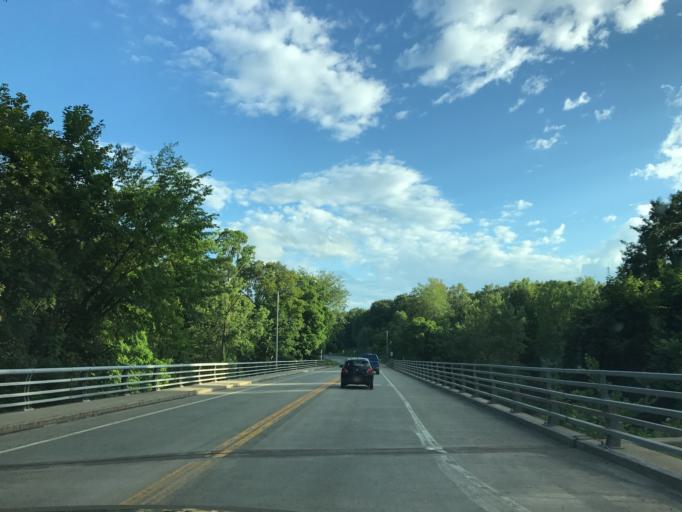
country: US
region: New York
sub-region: Saratoga County
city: Schuylerville
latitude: 43.0971
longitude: -73.5826
